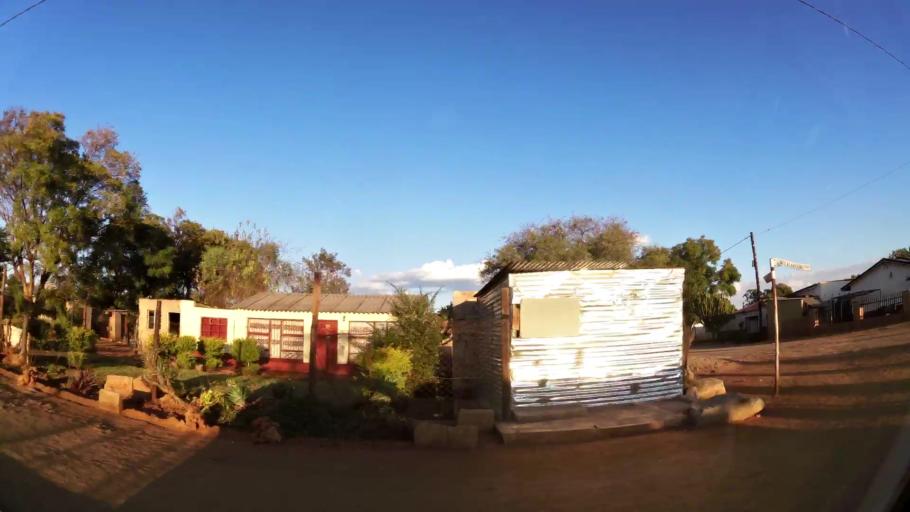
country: ZA
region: Limpopo
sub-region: Waterberg District Municipality
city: Mokopane
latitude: -24.1390
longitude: 28.9812
